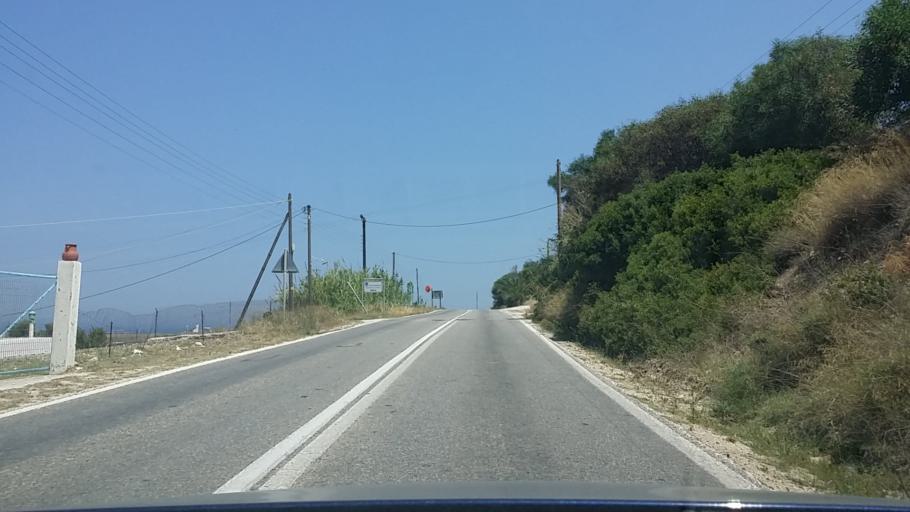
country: GR
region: South Aegean
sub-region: Nomos Kykladon
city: Antiparos
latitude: 37.0543
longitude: 25.1167
